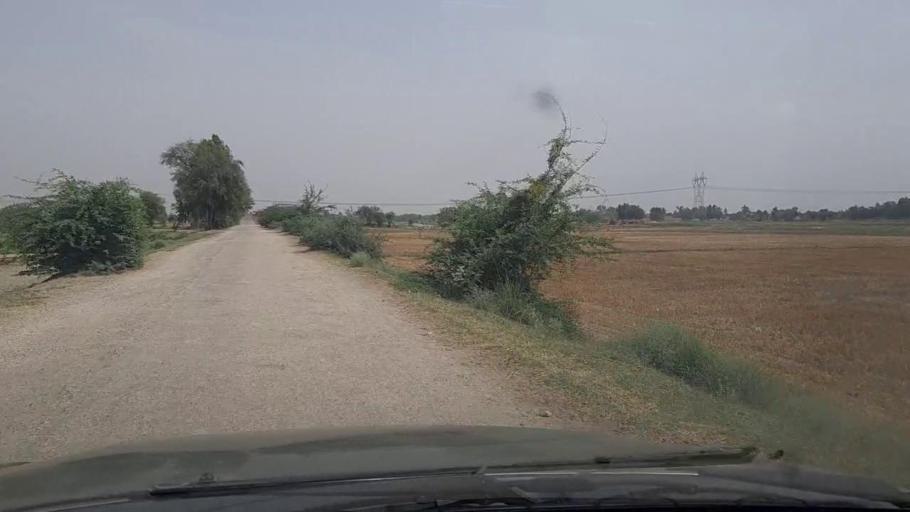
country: PK
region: Sindh
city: Shikarpur
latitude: 27.9178
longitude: 68.6831
